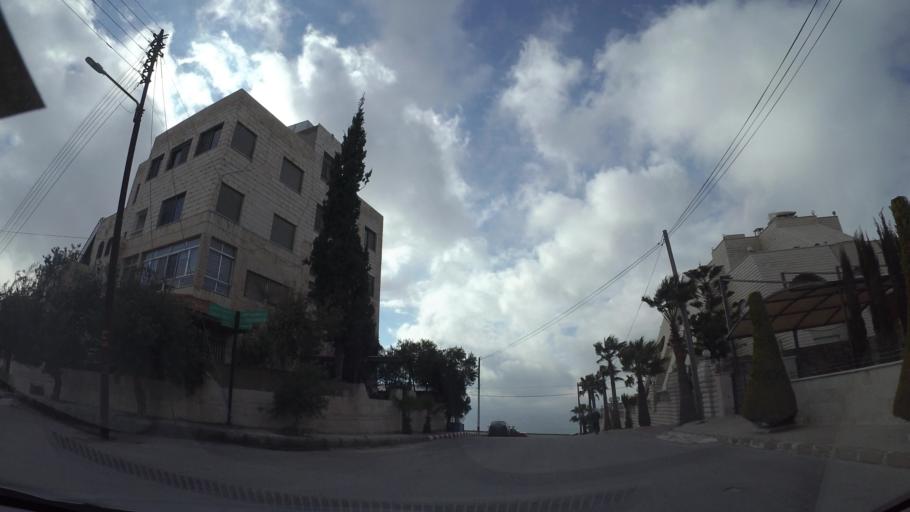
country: JO
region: Amman
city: Al Jubayhah
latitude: 32.0422
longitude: 35.8697
